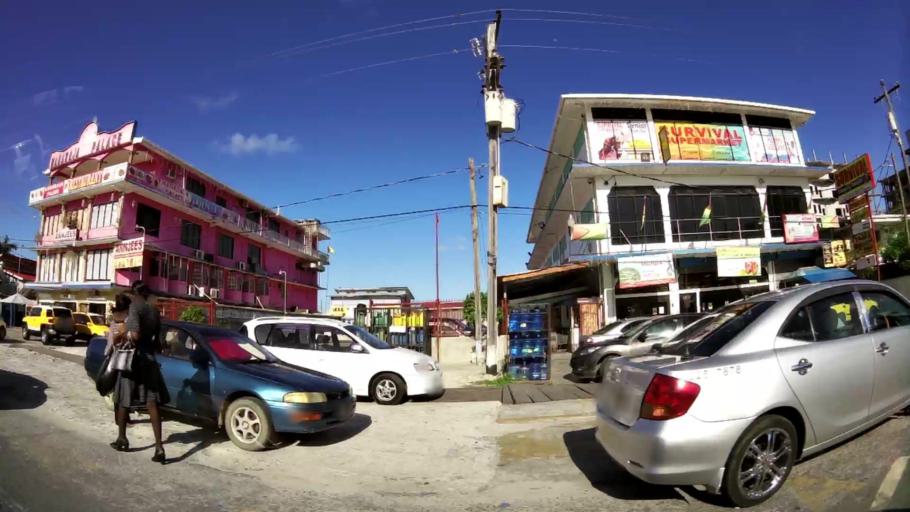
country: GY
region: Demerara-Mahaica
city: Georgetown
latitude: 6.8179
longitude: -58.1353
